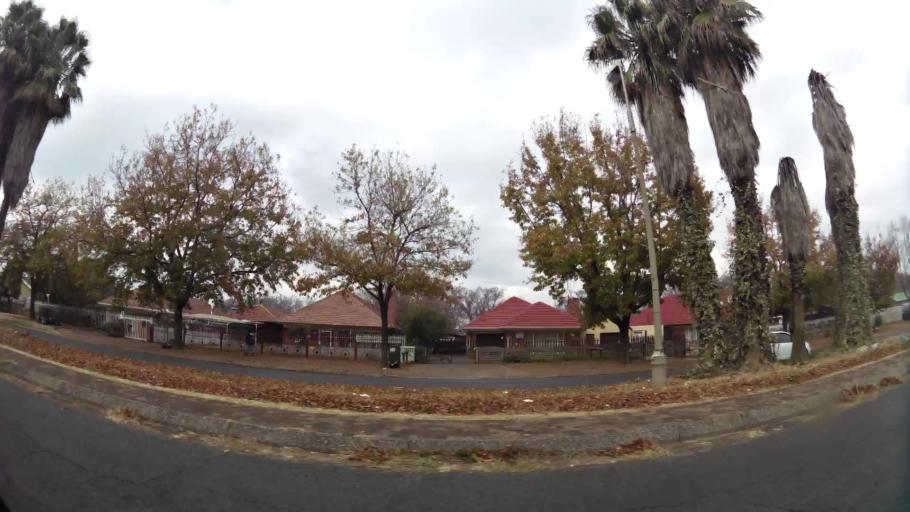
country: ZA
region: Gauteng
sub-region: Sedibeng District Municipality
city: Vanderbijlpark
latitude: -26.6967
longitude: 27.8457
